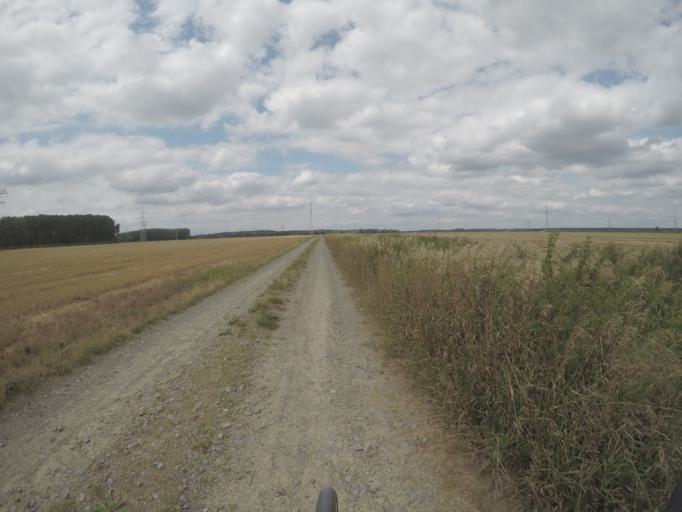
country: DE
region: Brandenburg
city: Falkensee
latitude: 52.6097
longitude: 13.0597
